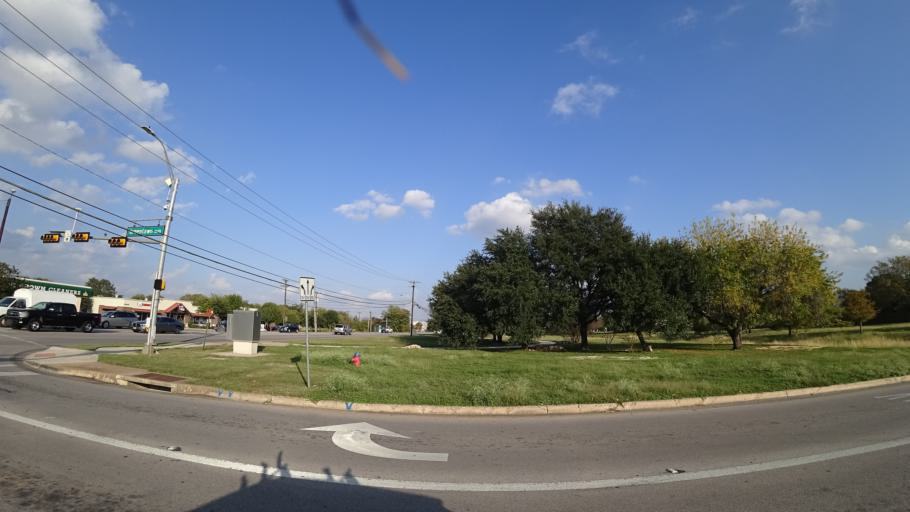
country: US
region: Texas
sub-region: Williamson County
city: Round Rock
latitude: 30.4959
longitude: -97.6652
